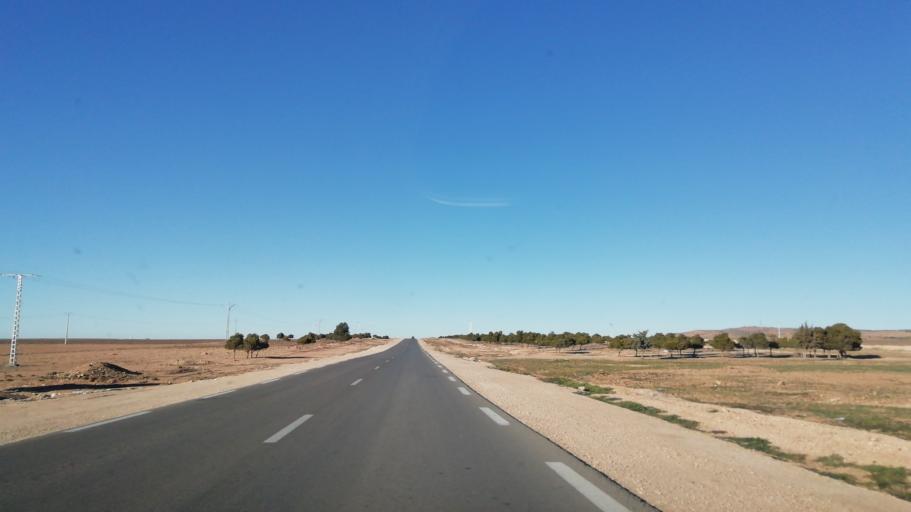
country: DZ
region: Tlemcen
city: Sebdou
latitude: 34.2396
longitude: -1.2568
